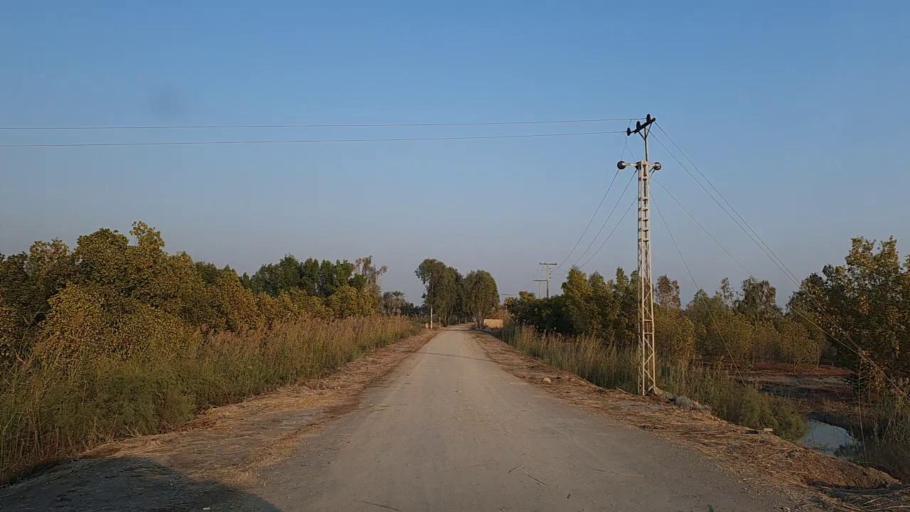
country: PK
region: Sindh
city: Bandhi
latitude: 26.5428
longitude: 68.3060
